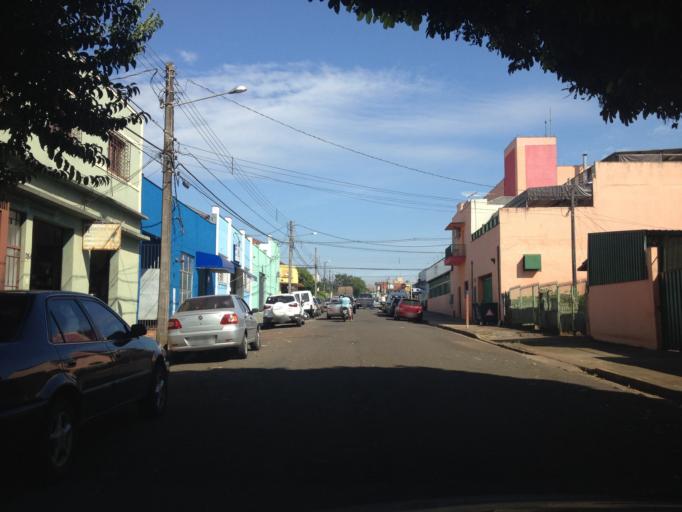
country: BR
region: Parana
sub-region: Londrina
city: Londrina
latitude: -23.2991
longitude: -51.1620
